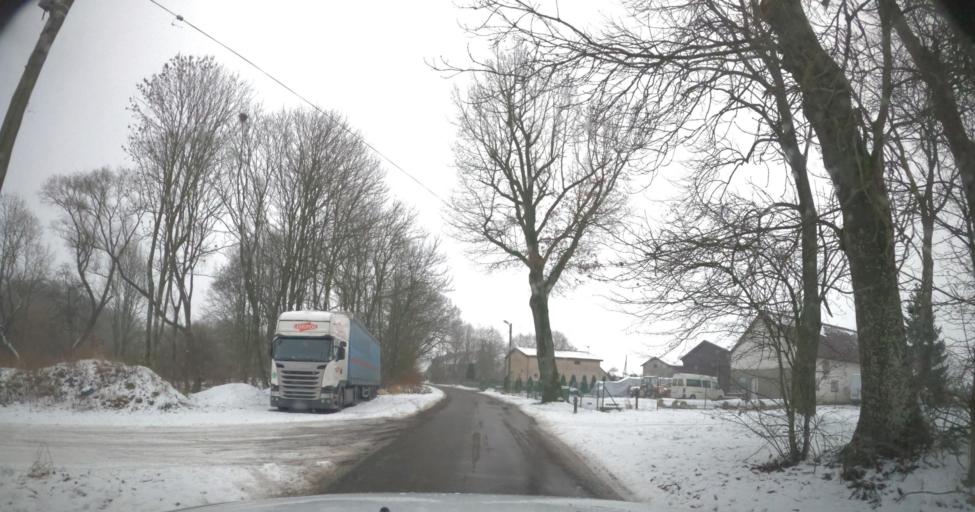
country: PL
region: West Pomeranian Voivodeship
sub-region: Powiat gryficki
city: Brojce
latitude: 53.9041
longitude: 15.3701
